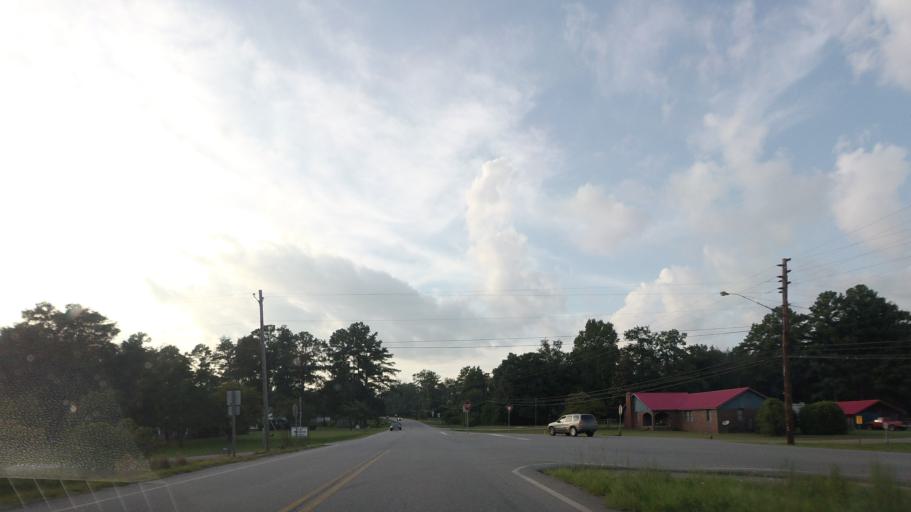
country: US
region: Georgia
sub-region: Wilkinson County
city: Gordon
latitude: 32.8841
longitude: -83.3443
